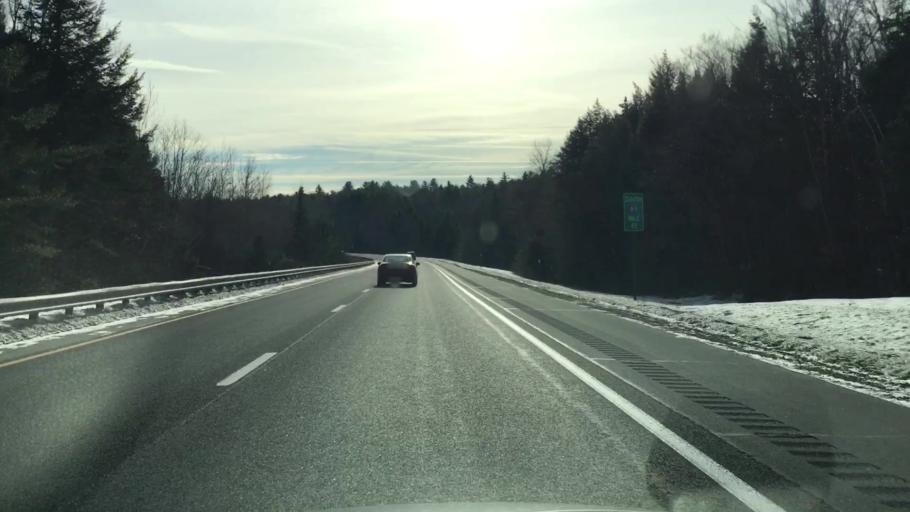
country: US
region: New Hampshire
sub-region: Sullivan County
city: Grantham
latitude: 43.5265
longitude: -72.1417
